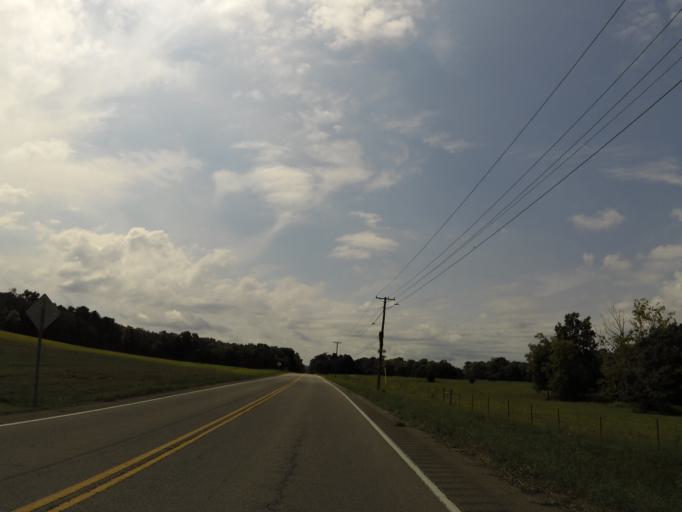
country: US
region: Tennessee
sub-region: Humphreys County
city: Waverly
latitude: 35.8657
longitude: -87.8096
